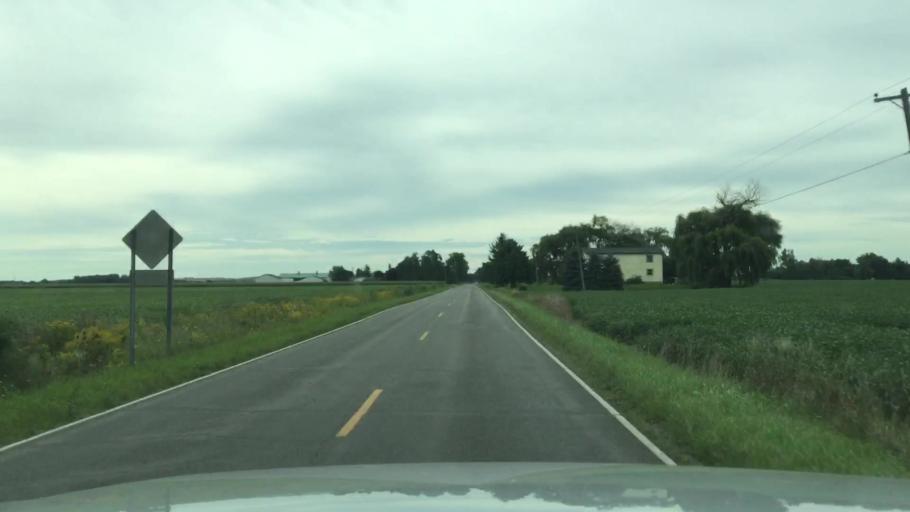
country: US
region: Michigan
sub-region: Shiawassee County
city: Durand
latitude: 43.0272
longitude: -83.9872
